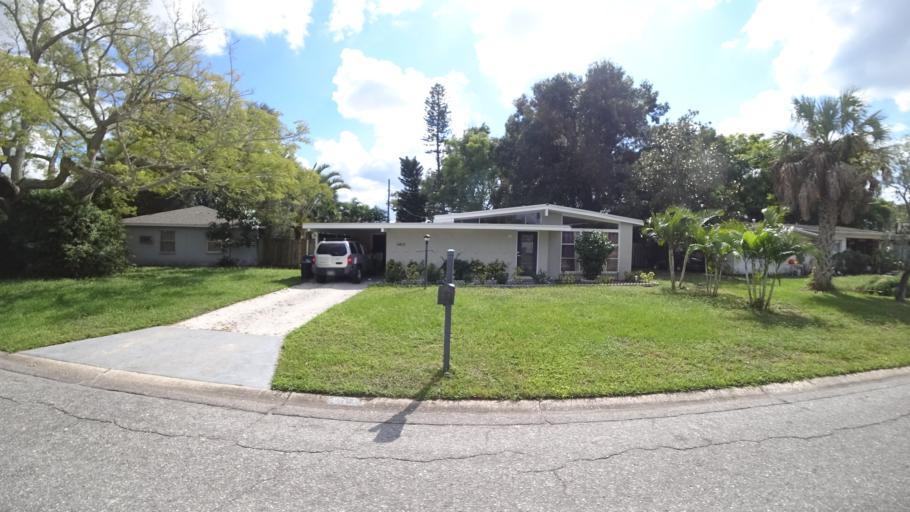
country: US
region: Florida
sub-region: Manatee County
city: Bayshore Gardens
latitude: 27.4268
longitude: -82.5860
